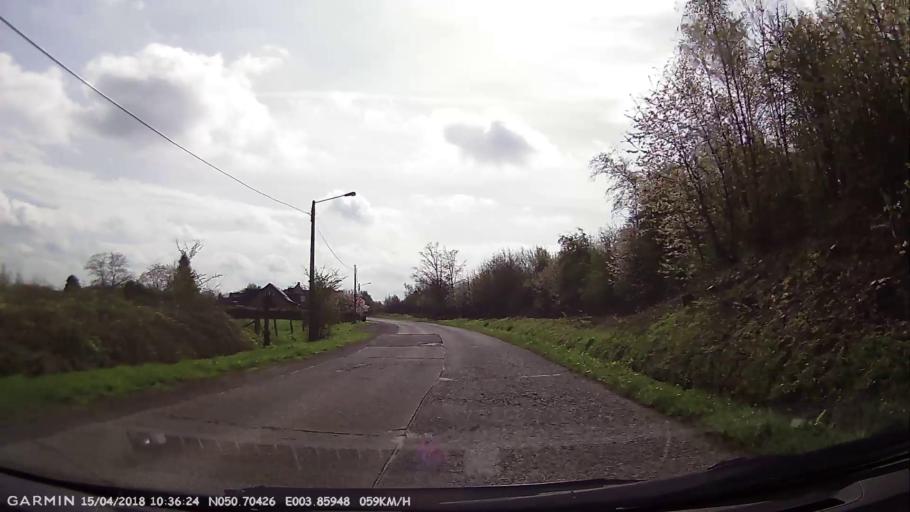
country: BE
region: Wallonia
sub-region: Province du Hainaut
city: Lessines
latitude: 50.7042
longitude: 3.8596
